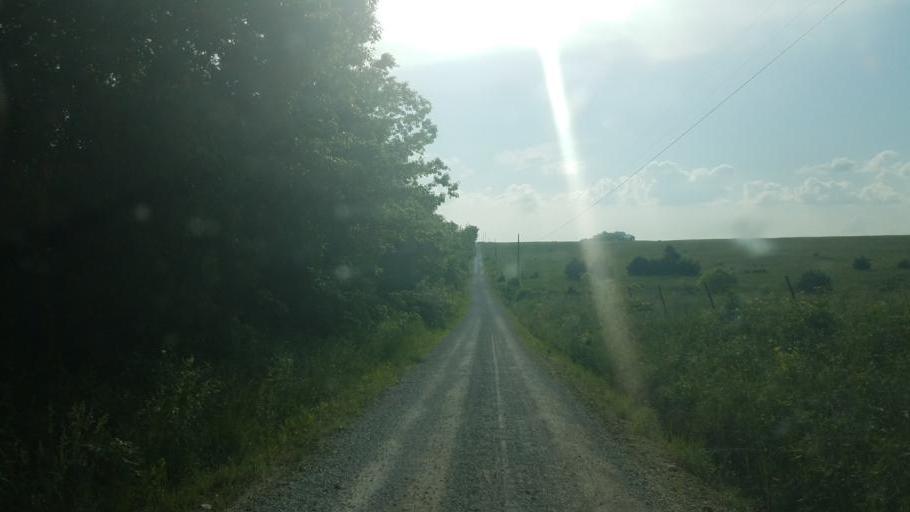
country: US
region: Missouri
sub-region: Moniteau County
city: California
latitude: 38.7527
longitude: -92.6077
